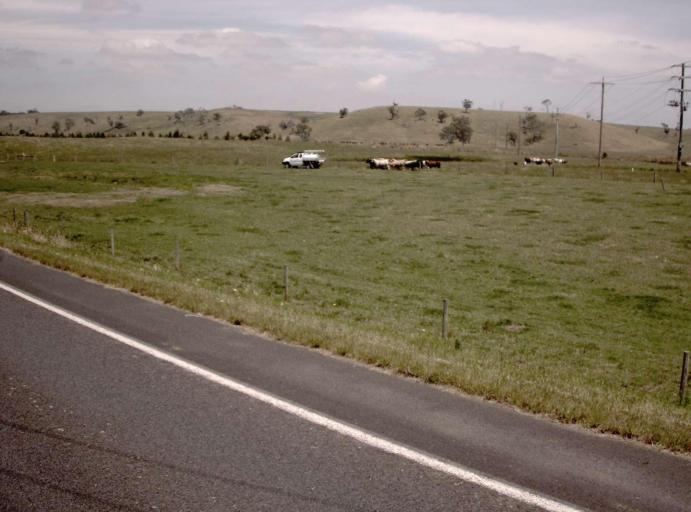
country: AU
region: Victoria
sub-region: Latrobe
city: Traralgon
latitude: -38.2209
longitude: 146.5460
